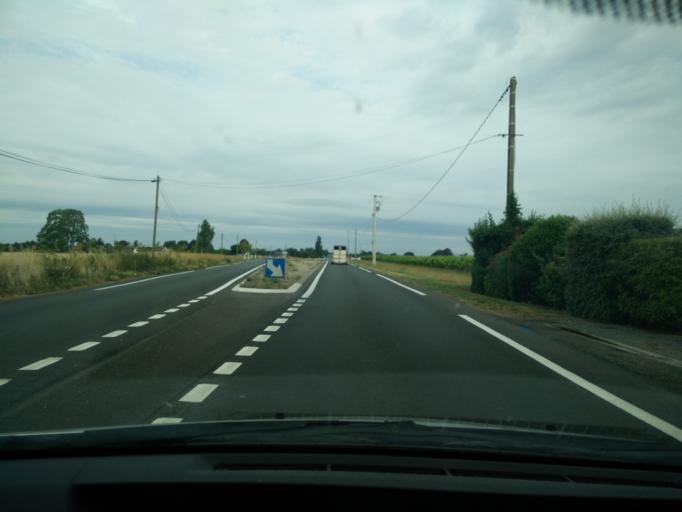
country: FR
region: Pays de la Loire
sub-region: Departement de Maine-et-Loire
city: Brissac-Quince
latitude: 47.3250
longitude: -0.4154
